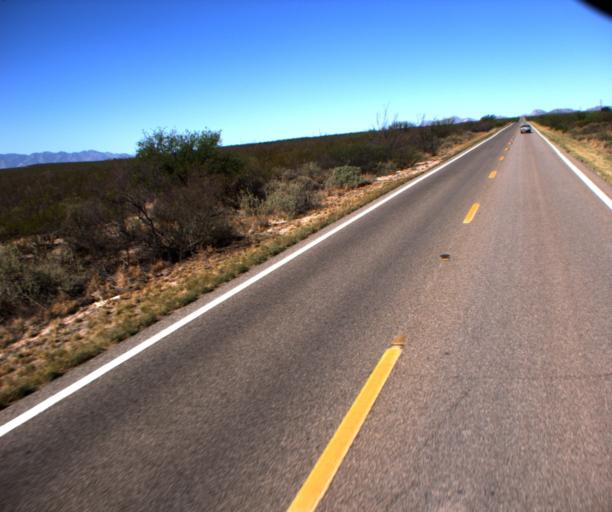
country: US
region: Arizona
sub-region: Cochise County
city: Tombstone
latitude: 31.7211
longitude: -110.2158
